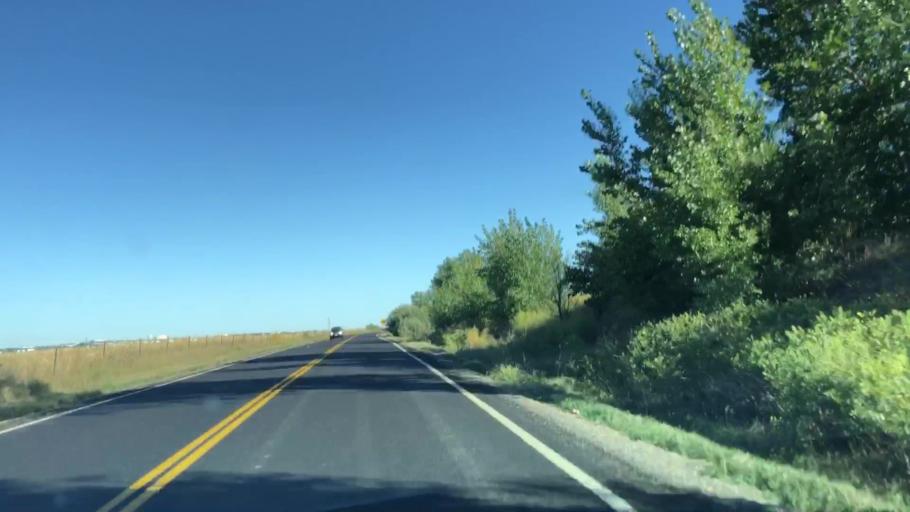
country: US
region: Colorado
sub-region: Larimer County
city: Loveland
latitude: 40.4643
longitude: -105.0526
